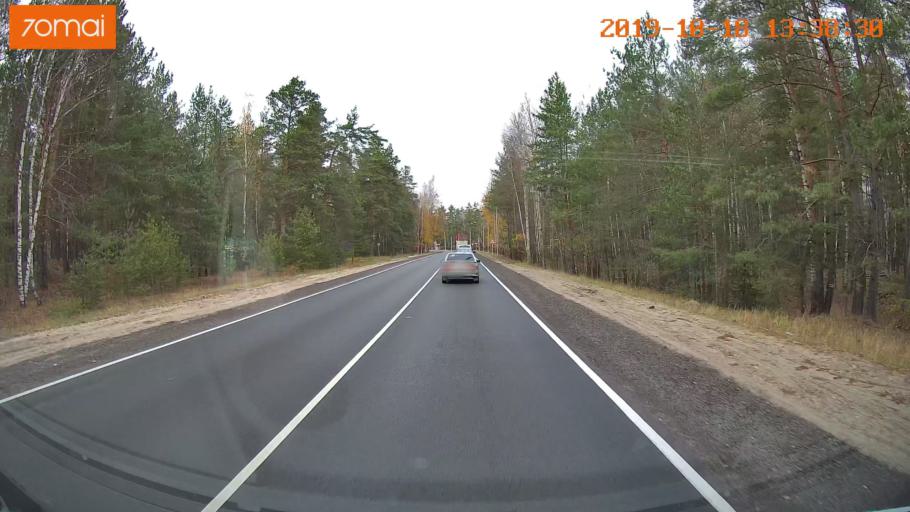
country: RU
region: Rjazan
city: Solotcha
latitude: 54.8908
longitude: 40.0028
